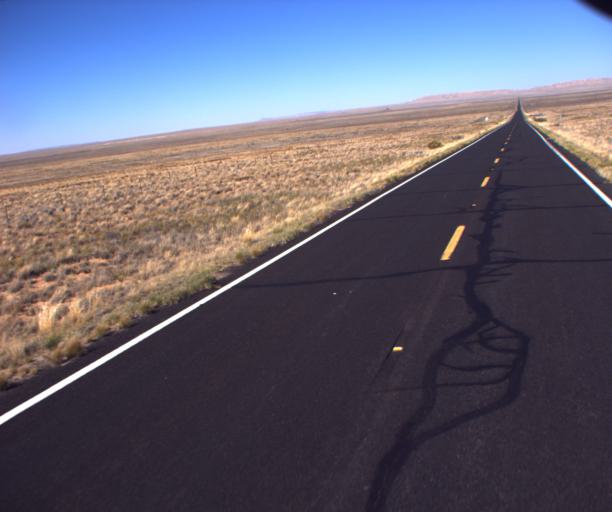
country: US
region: Arizona
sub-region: Navajo County
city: First Mesa
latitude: 35.6664
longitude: -110.4951
